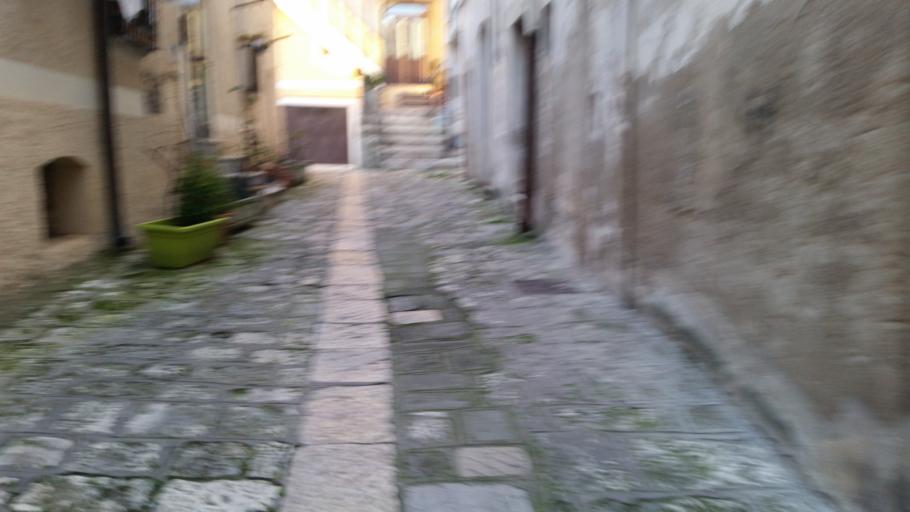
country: IT
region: Basilicate
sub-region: Provincia di Matera
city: Tricarico
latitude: 40.6231
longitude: 16.1441
